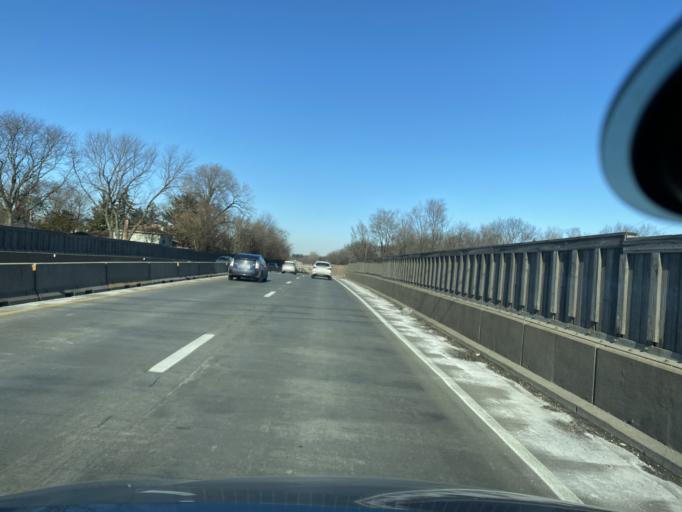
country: US
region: Illinois
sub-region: DuPage County
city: Clarendon Hills
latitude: 41.7987
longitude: -87.9466
